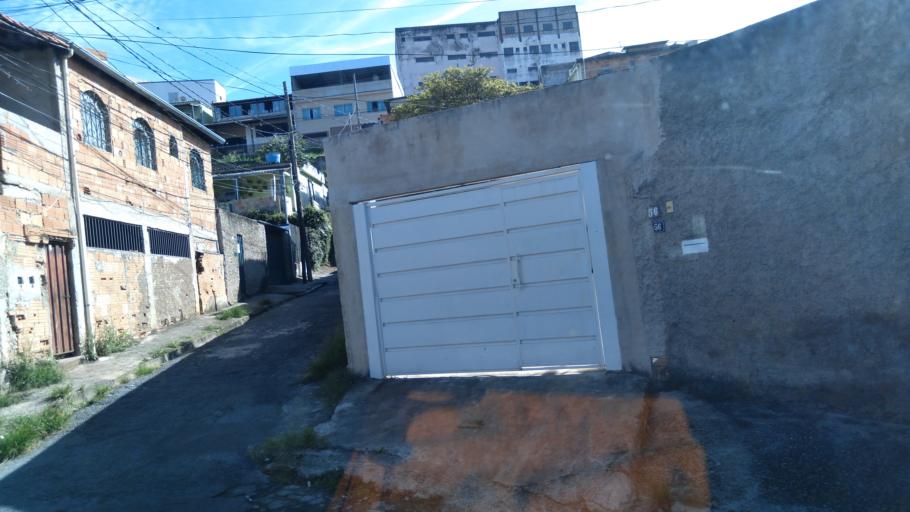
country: BR
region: Minas Gerais
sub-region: Contagem
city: Contagem
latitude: -19.9057
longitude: -44.0025
